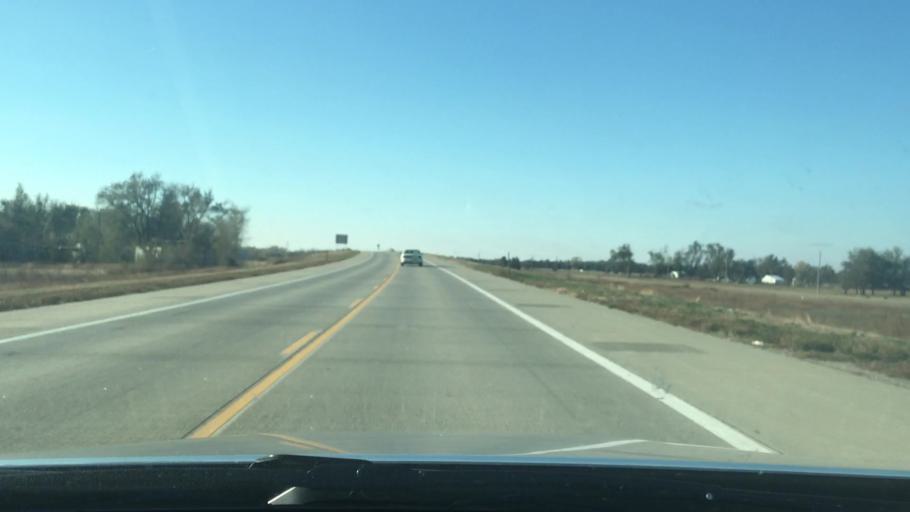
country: US
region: Kansas
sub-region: Reno County
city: Nickerson
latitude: 38.1005
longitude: -98.0106
